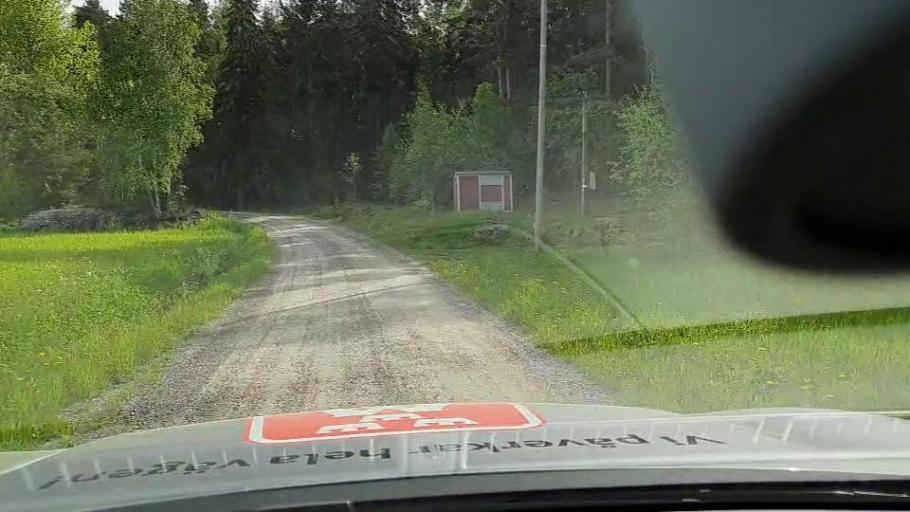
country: SE
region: Soedermanland
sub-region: Eskilstuna Kommun
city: Arla
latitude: 59.2619
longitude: 16.8418
